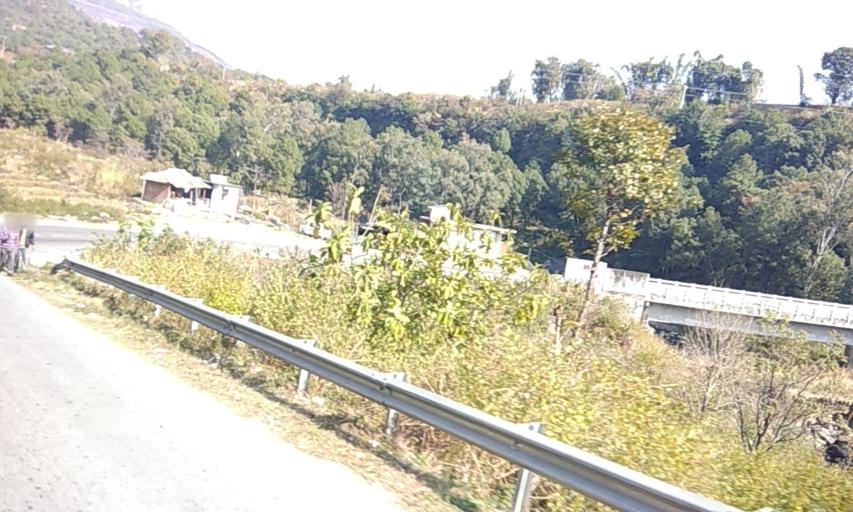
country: IN
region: Himachal Pradesh
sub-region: Kangra
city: Dharmsala
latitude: 32.1615
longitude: 76.4062
